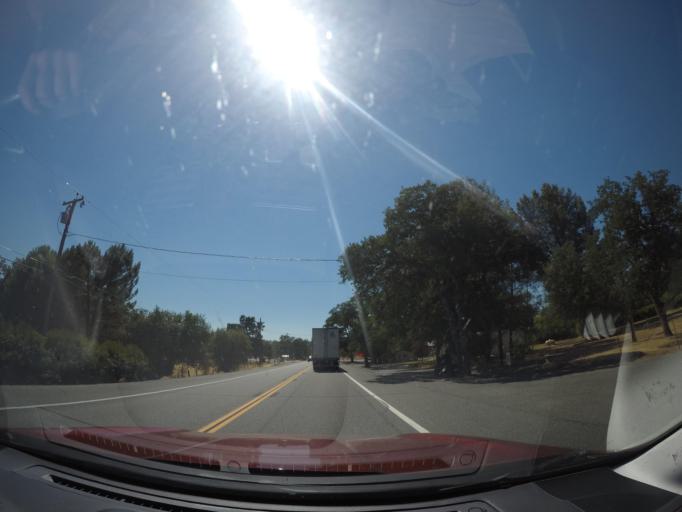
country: US
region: California
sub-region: Shasta County
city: Bella Vista
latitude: 40.6393
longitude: -122.2364
